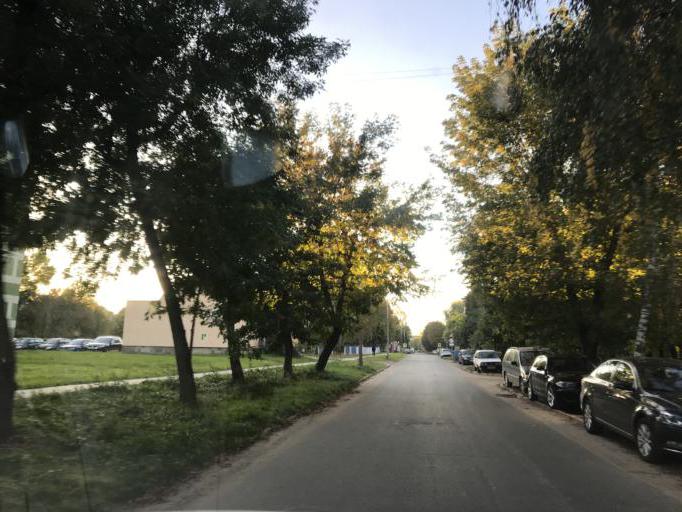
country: BY
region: Mogilev
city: Mahilyow
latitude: 53.9064
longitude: 30.3216
